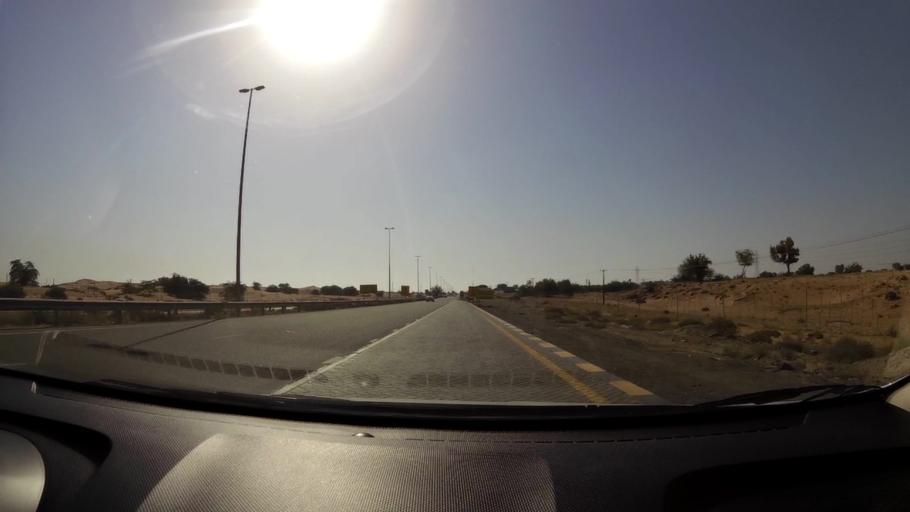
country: AE
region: Umm al Qaywayn
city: Umm al Qaywayn
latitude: 25.4647
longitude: 55.5964
